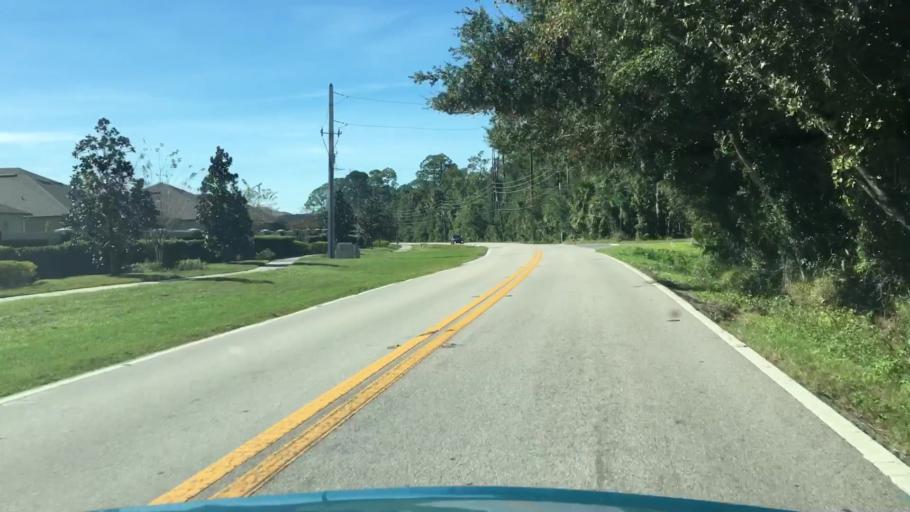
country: US
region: Florida
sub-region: Seminole County
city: Heathrow
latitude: 28.8248
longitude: -81.3553
